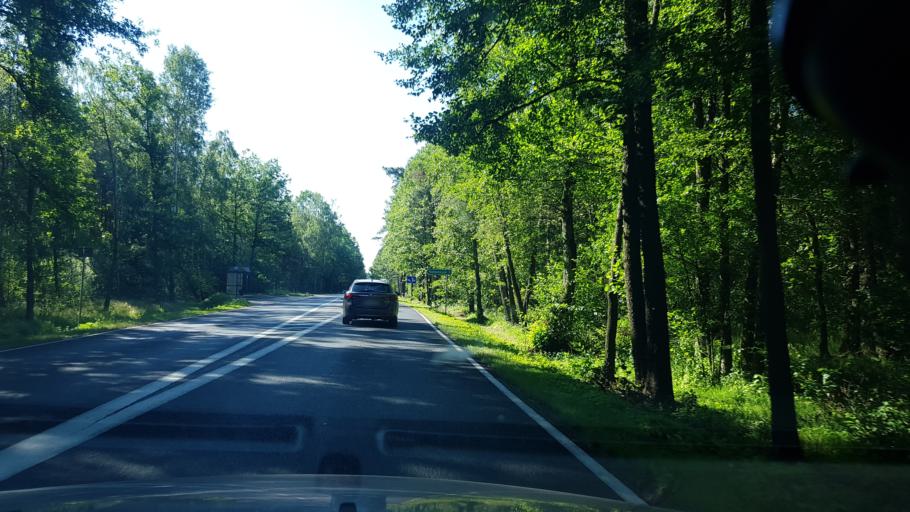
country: PL
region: Masovian Voivodeship
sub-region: Powiat wyszkowski
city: Branszczyk
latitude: 52.5774
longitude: 21.5362
